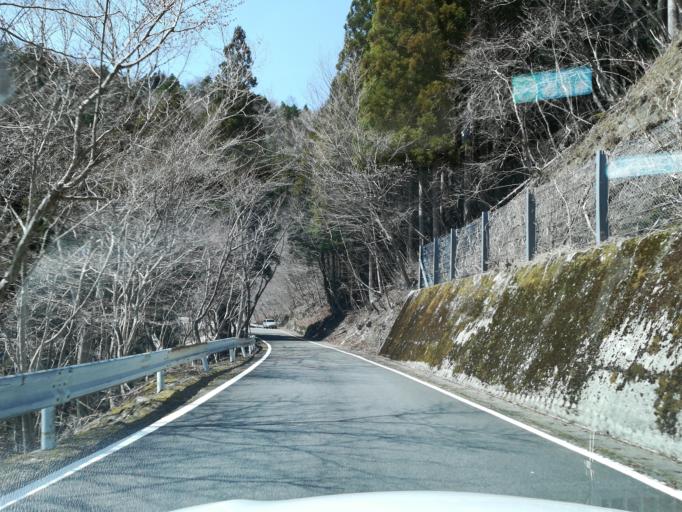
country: JP
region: Tokushima
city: Wakimachi
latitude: 33.8529
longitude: 134.0351
